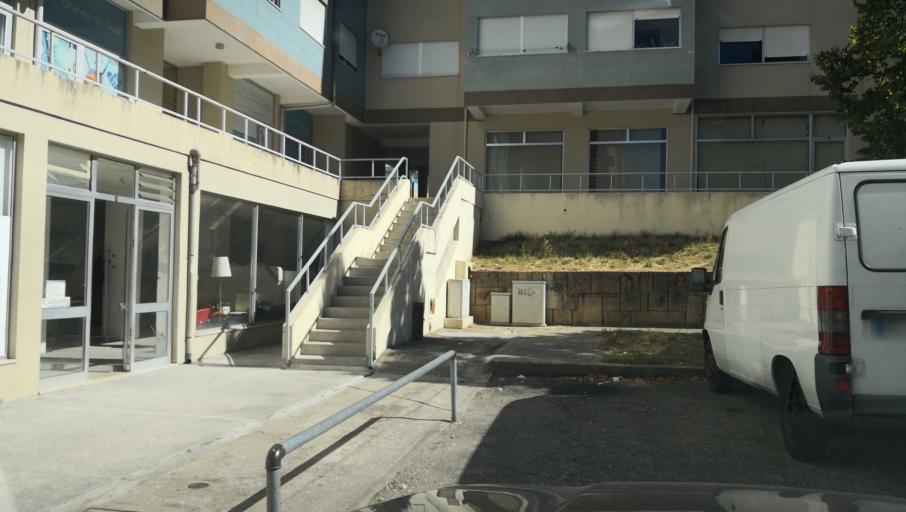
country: PT
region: Vila Real
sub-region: Vila Real
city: Vila Real
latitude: 41.3061
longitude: -7.7455
